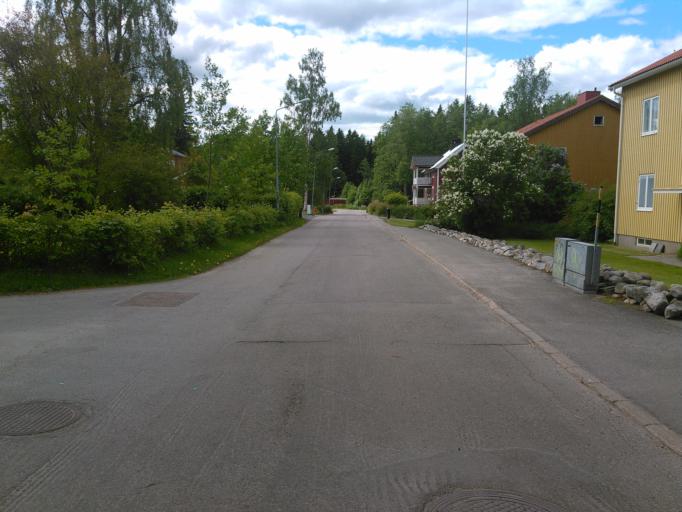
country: SE
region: Vaesterbotten
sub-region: Umea Kommun
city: Umea
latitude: 63.8235
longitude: 20.2419
